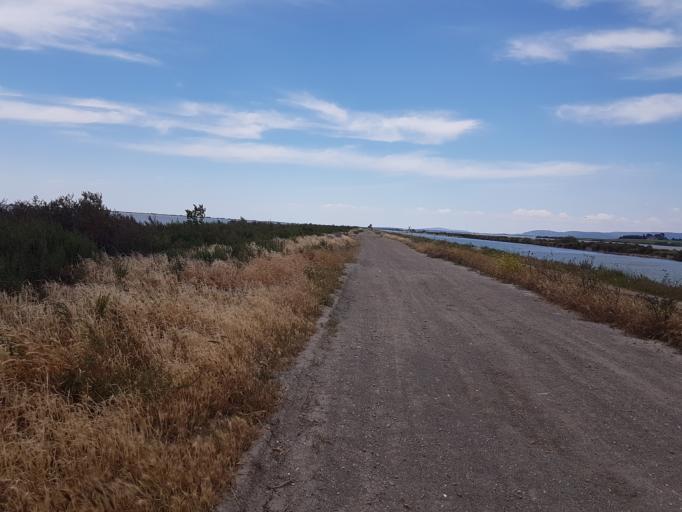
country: FR
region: Languedoc-Roussillon
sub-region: Departement de l'Herault
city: Villeneuve-les-Maguelone
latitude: 43.5130
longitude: 3.8755
